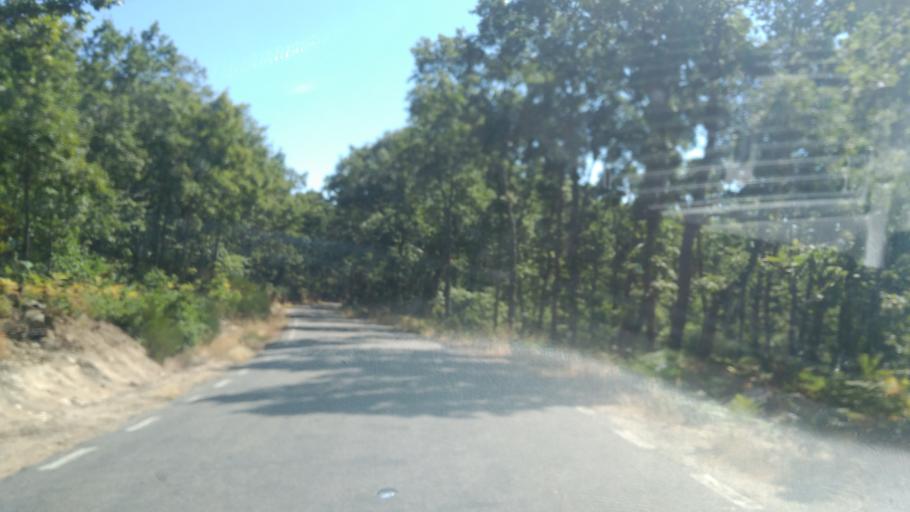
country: ES
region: Castille and Leon
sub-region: Provincia de Salamanca
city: San Martin del Castanar
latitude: 40.5258
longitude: -6.0845
